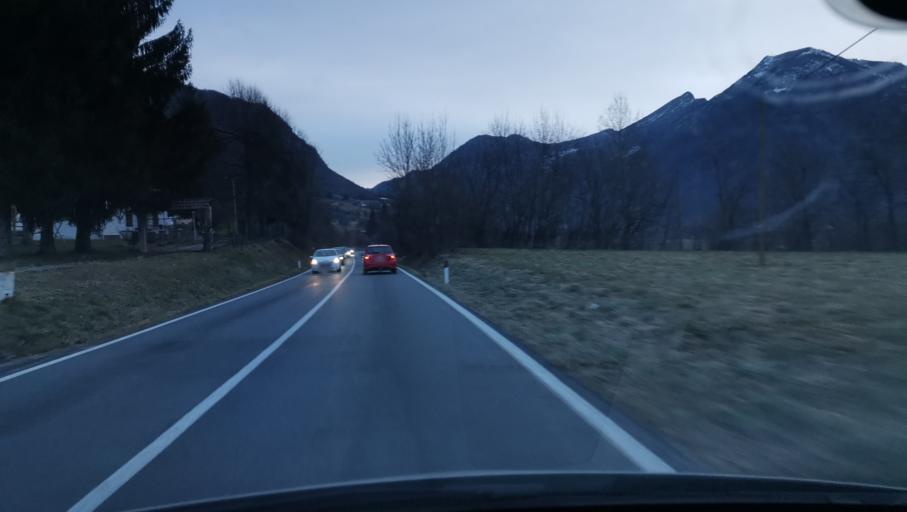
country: IT
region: Piedmont
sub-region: Provincia di Cuneo
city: Demonte
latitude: 44.3138
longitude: 7.3330
